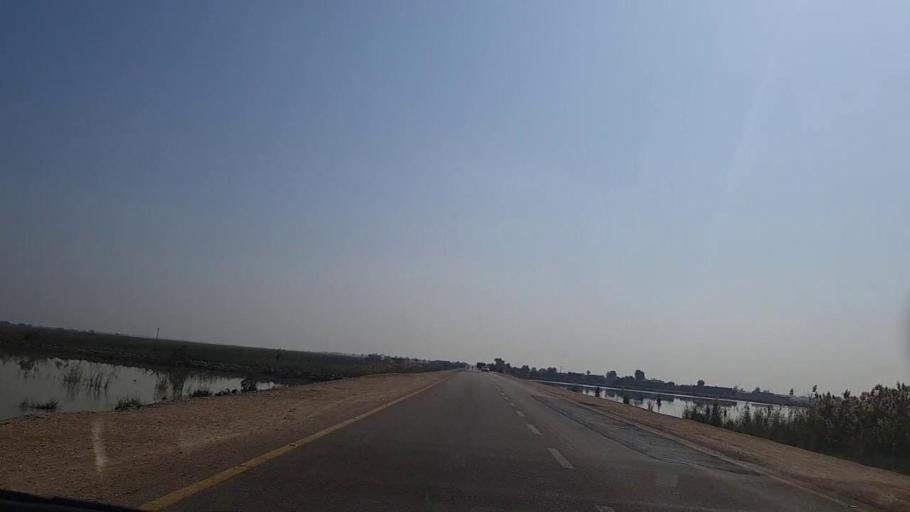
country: PK
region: Sindh
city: Sakrand
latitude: 26.0784
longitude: 68.4035
